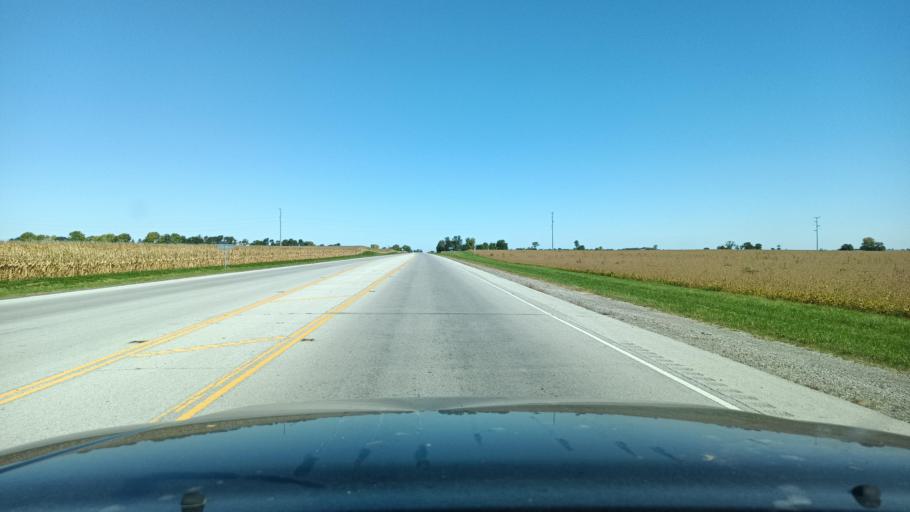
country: US
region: Illinois
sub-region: Champaign County
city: Philo
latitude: 40.0119
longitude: -88.1614
